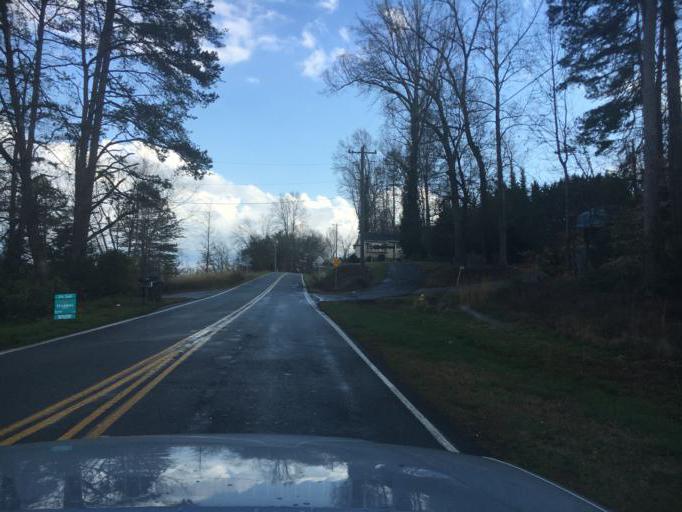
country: US
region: South Carolina
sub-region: Greenville County
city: Parker
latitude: 34.8346
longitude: -82.4910
